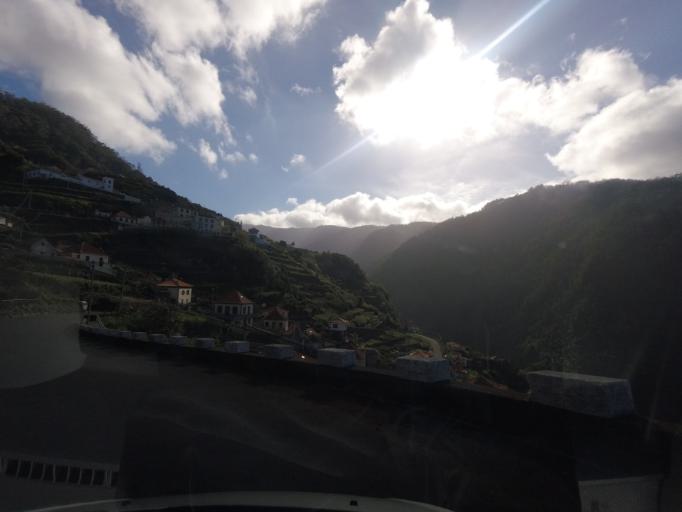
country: PT
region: Madeira
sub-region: Porto Moniz
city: Porto Moniz
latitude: 32.8492
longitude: -17.1573
